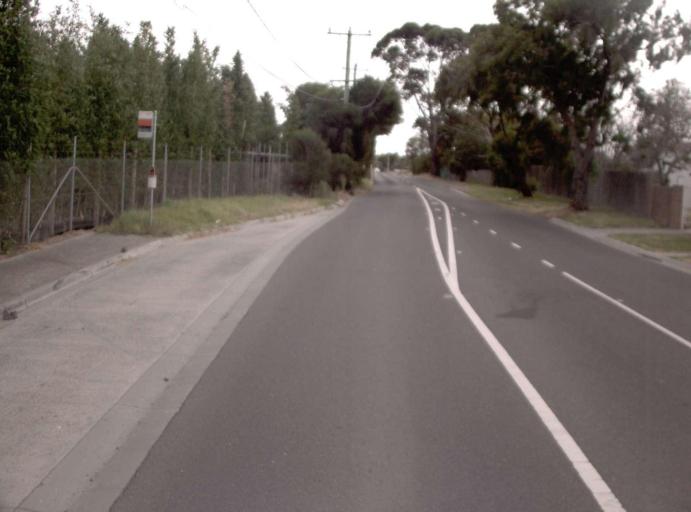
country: AU
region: Victoria
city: Heatherton
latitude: -37.9463
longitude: 145.0968
